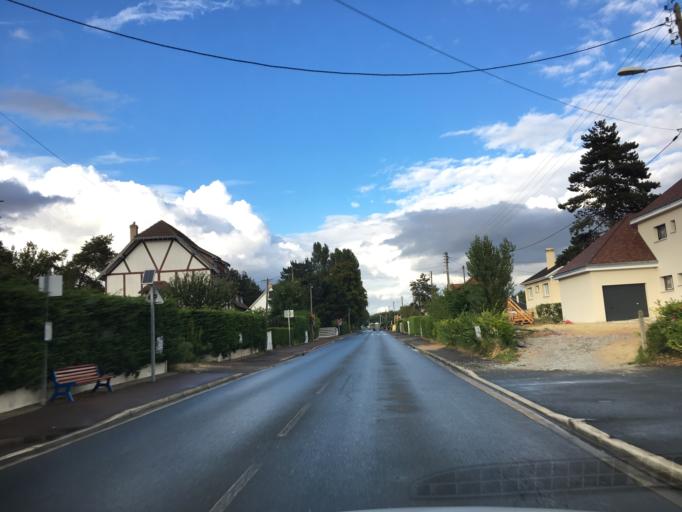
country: FR
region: Lower Normandy
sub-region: Departement du Calvados
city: Merville-Franceville-Plage
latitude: 49.2812
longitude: -0.1963
